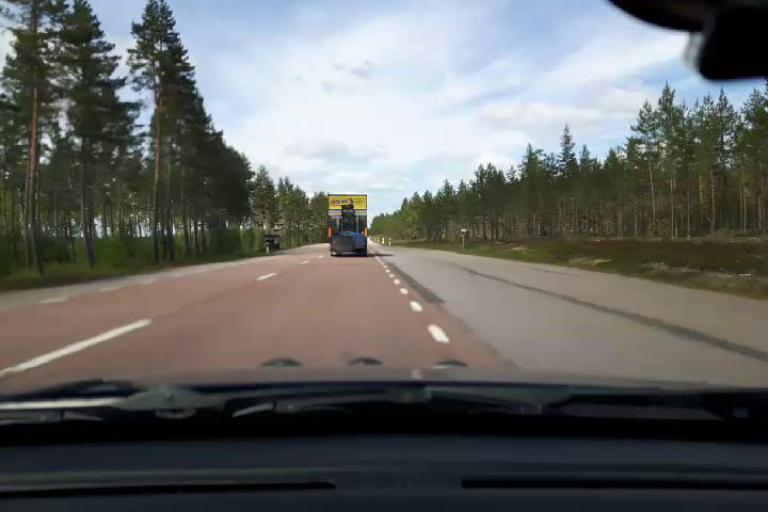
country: SE
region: Uppsala
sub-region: Osthammars Kommun
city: Bjorklinge
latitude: 60.1746
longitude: 17.4853
